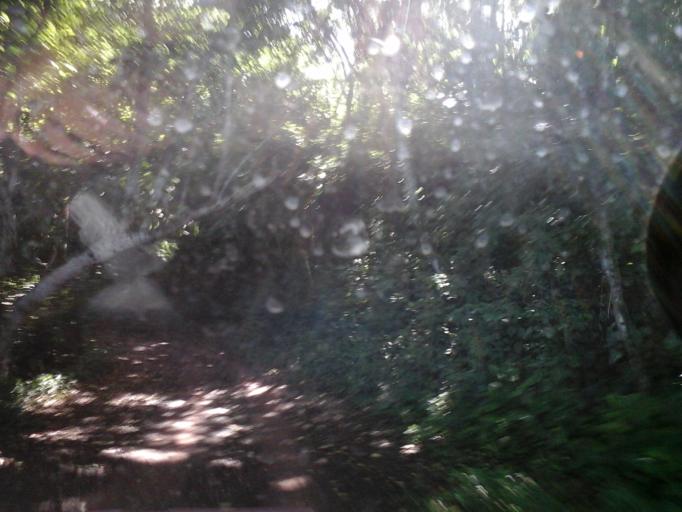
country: CO
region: Cesar
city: San Diego
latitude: 10.2593
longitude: -73.1091
